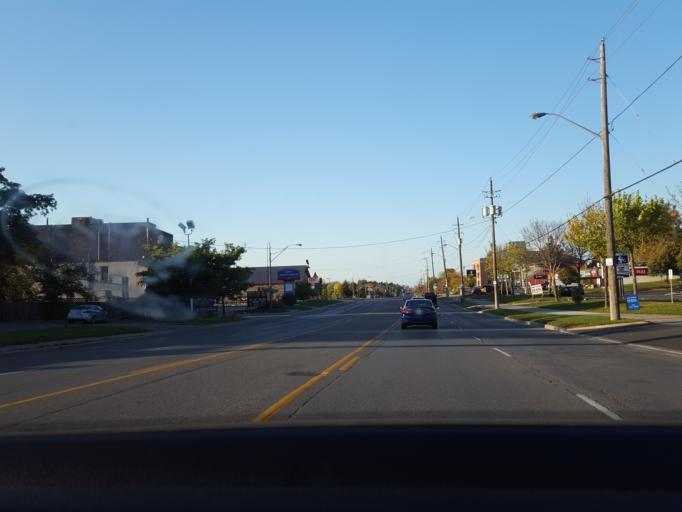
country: CA
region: Ontario
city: Newmarket
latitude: 44.0052
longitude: -79.4689
